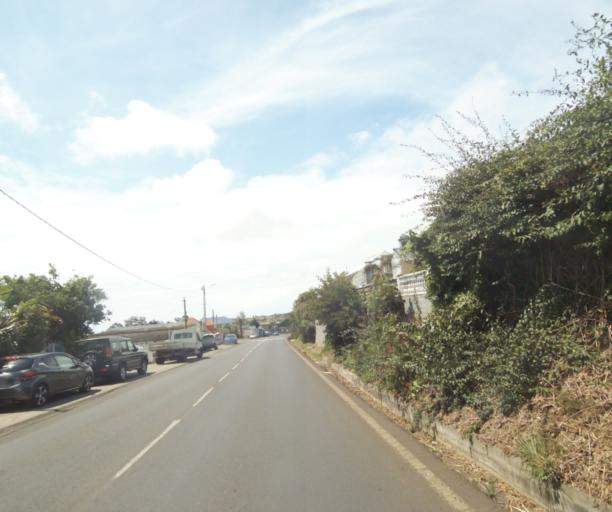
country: RE
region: Reunion
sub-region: Reunion
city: Trois-Bassins
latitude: -21.0743
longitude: 55.2675
